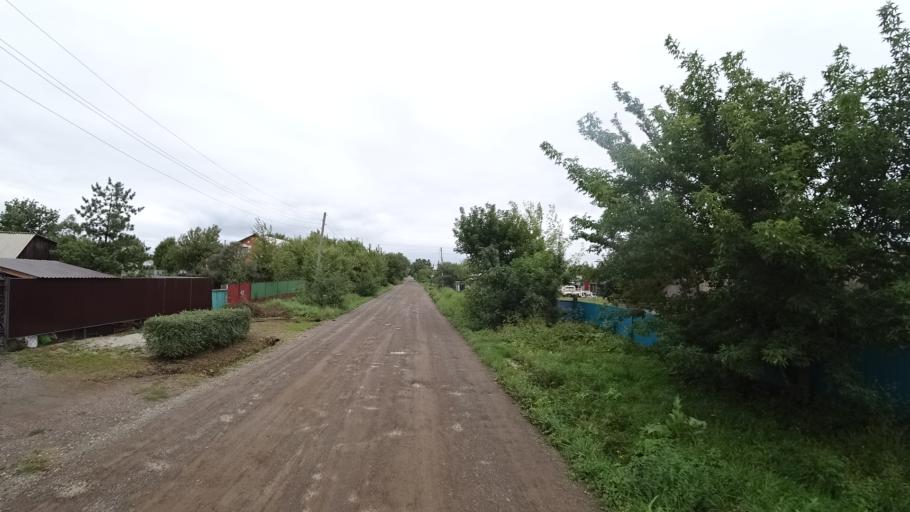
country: RU
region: Primorskiy
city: Chernigovka
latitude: 44.3376
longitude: 132.5650
